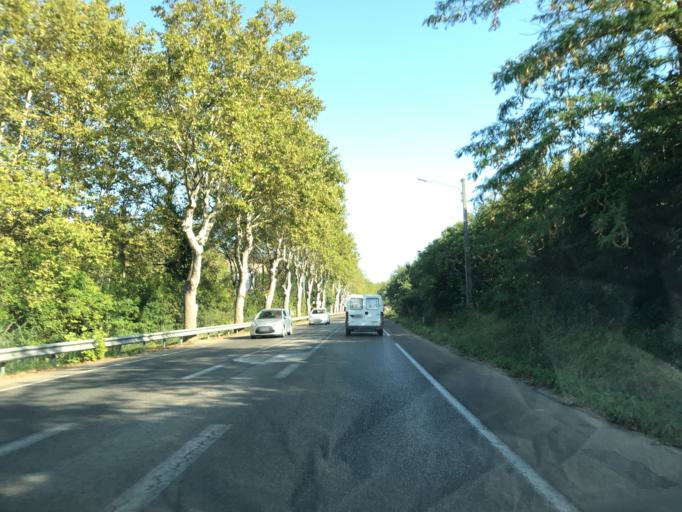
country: FR
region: Provence-Alpes-Cote d'Azur
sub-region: Departement des Bouches-du-Rhone
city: Saint-Chamas
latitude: 43.5698
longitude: 5.0217
